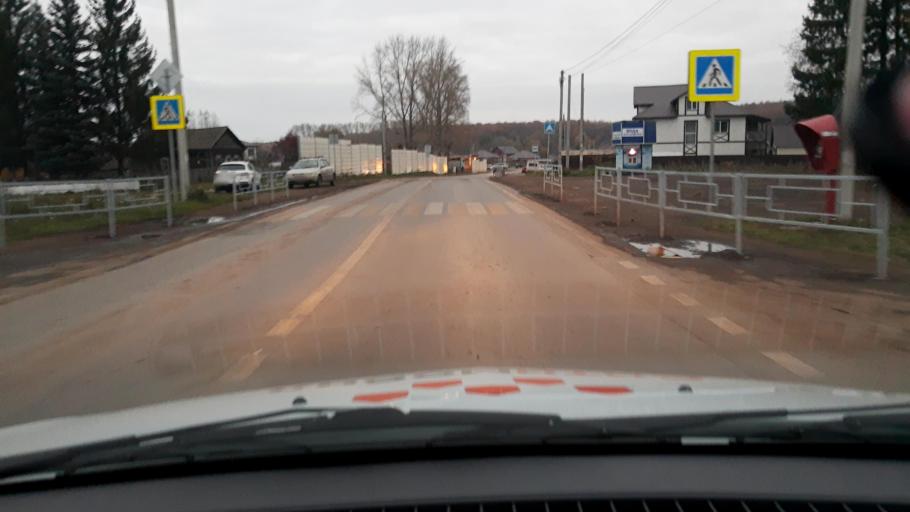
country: RU
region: Bashkortostan
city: Kabakovo
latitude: 54.6892
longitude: 56.1348
